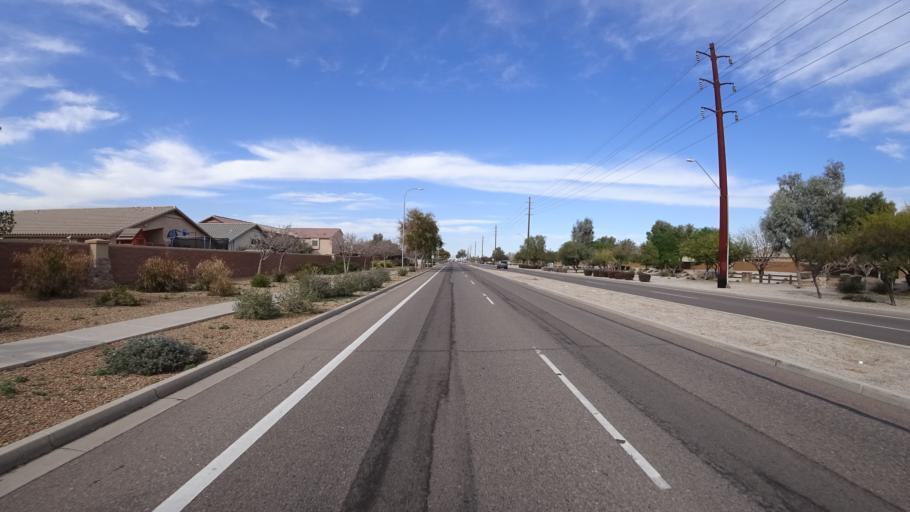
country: US
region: Arizona
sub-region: Maricopa County
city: Tolleson
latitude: 33.4166
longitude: -112.2556
